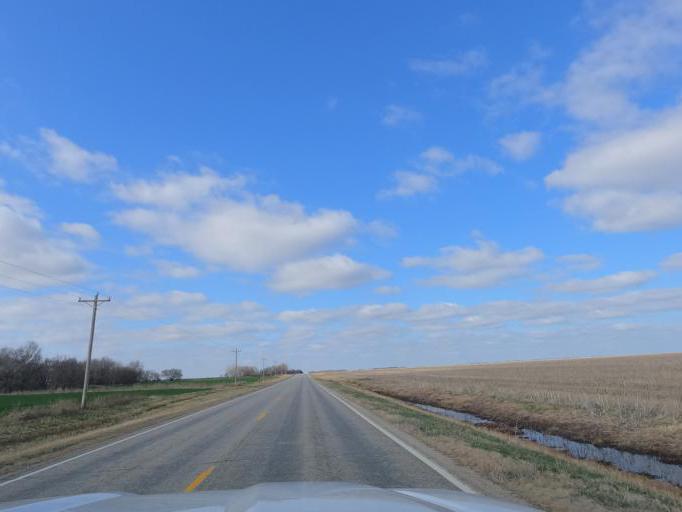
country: US
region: Kansas
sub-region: McPherson County
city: Inman
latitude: 38.1893
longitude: -97.8485
